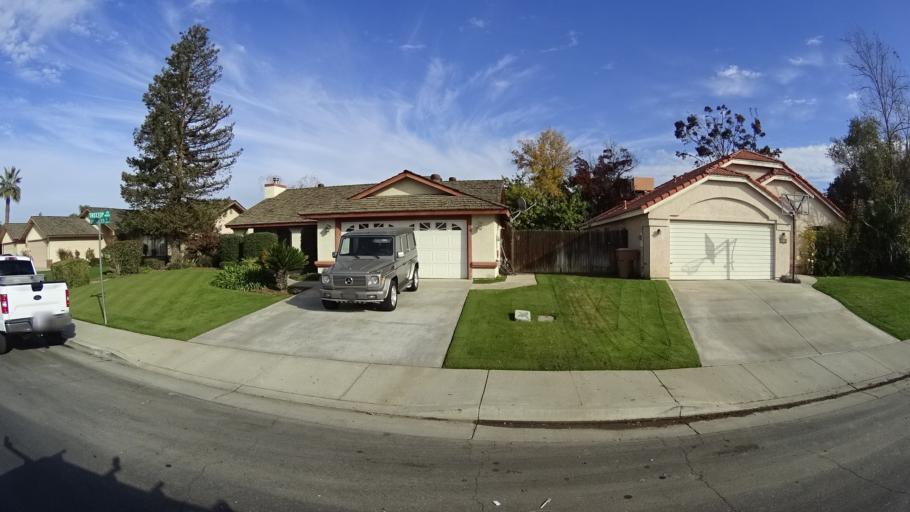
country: US
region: California
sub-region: Kern County
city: Greenacres
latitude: 35.3952
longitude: -119.1107
